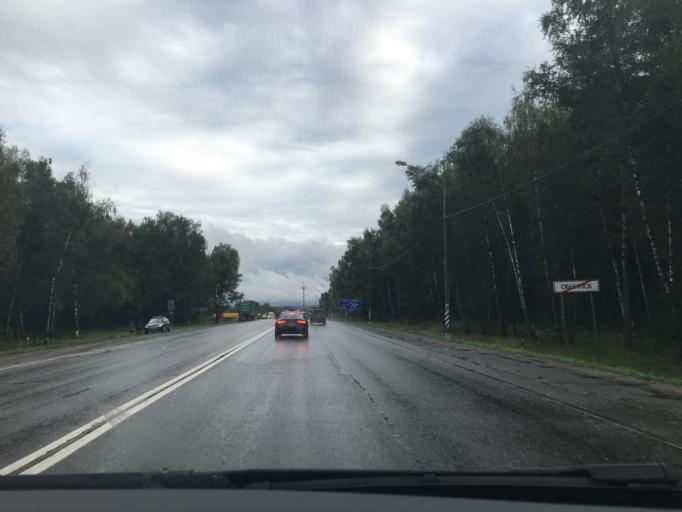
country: RU
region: Kaluga
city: Obninsk
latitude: 55.0818
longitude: 36.6305
